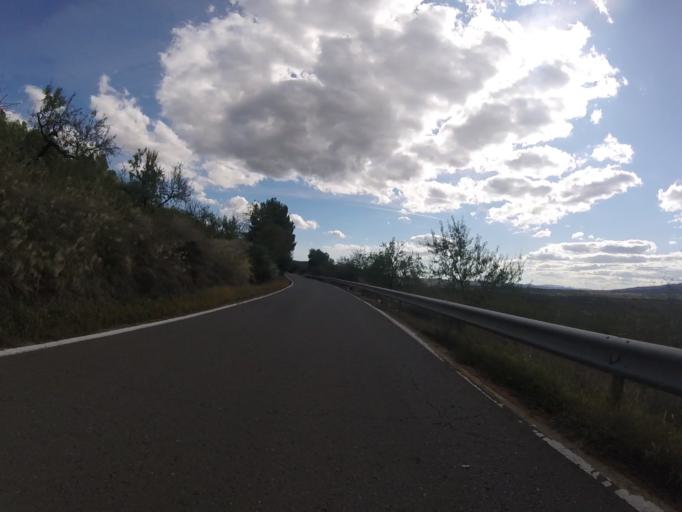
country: ES
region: Valencia
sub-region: Provincia de Castello
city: Cuevas de Vinroma
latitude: 40.3649
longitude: 0.1213
